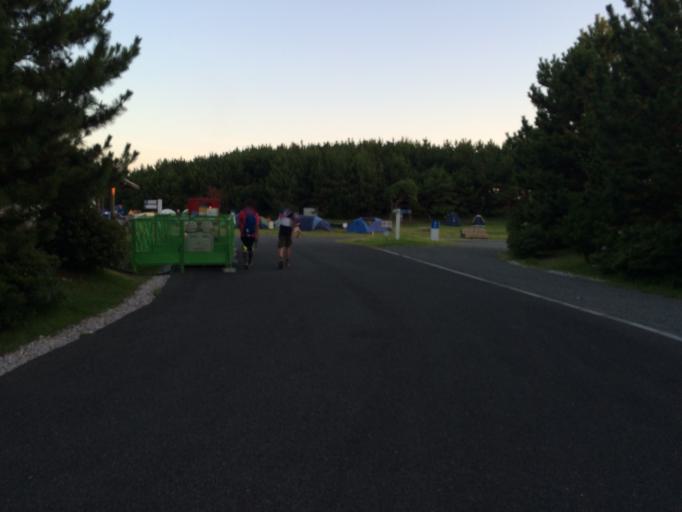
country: JP
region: Yamaguchi
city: Ogori-shimogo
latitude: 34.0076
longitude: 131.3748
